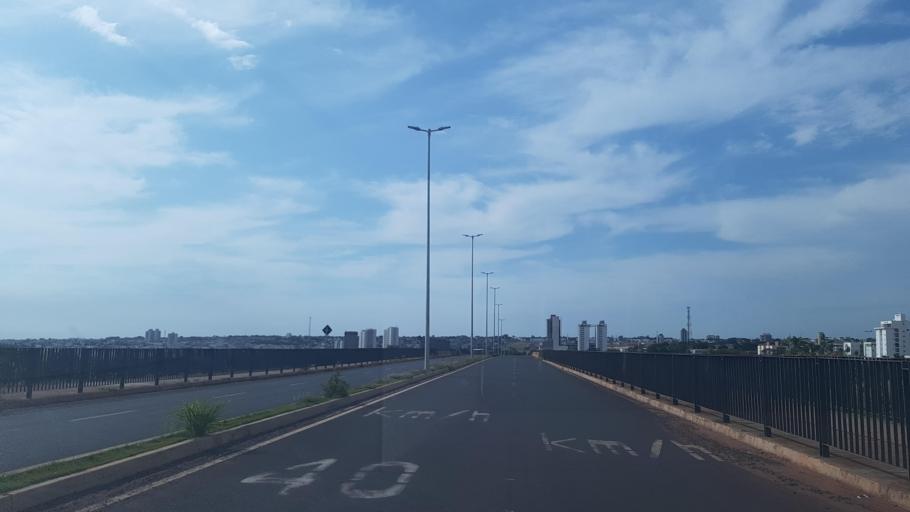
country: BR
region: Minas Gerais
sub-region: Uberlandia
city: Uberlandia
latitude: -18.8760
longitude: -48.2571
